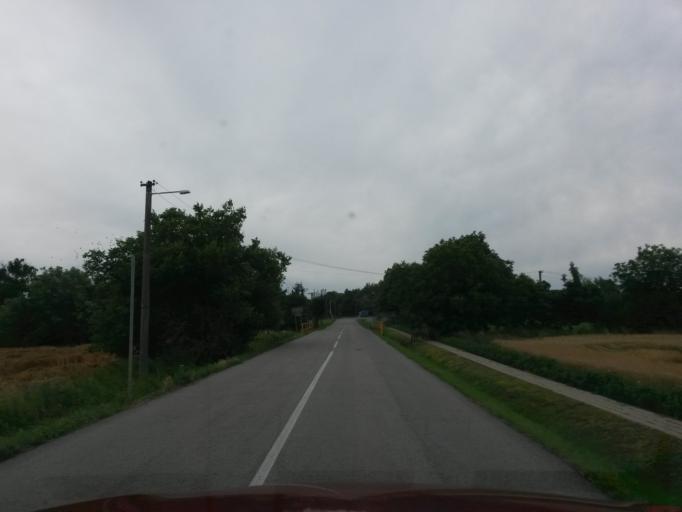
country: SK
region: Nitriansky
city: Tlmace
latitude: 48.1590
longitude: 18.4508
